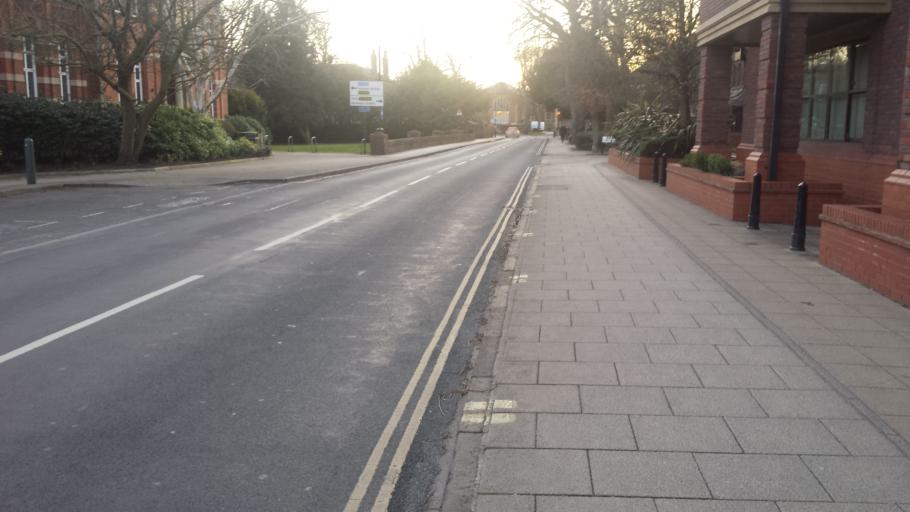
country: GB
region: England
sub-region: East Riding of Yorkshire
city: Beverley
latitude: 53.8406
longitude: -0.4300
